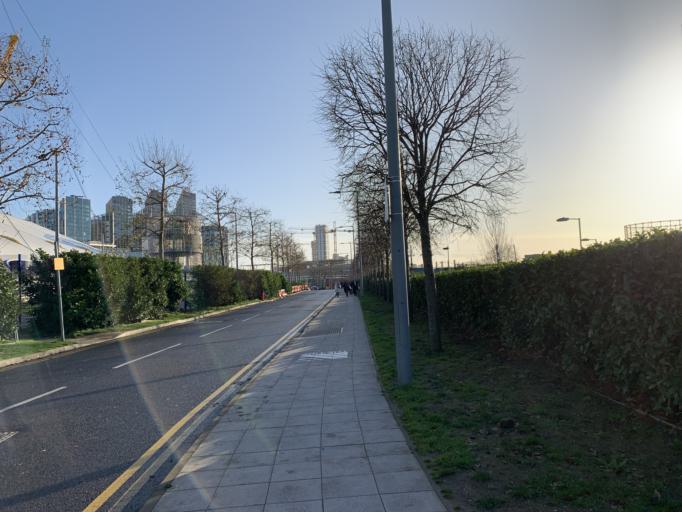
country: GB
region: England
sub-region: Greater London
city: Poplar
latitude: 51.5019
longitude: 0.0003
